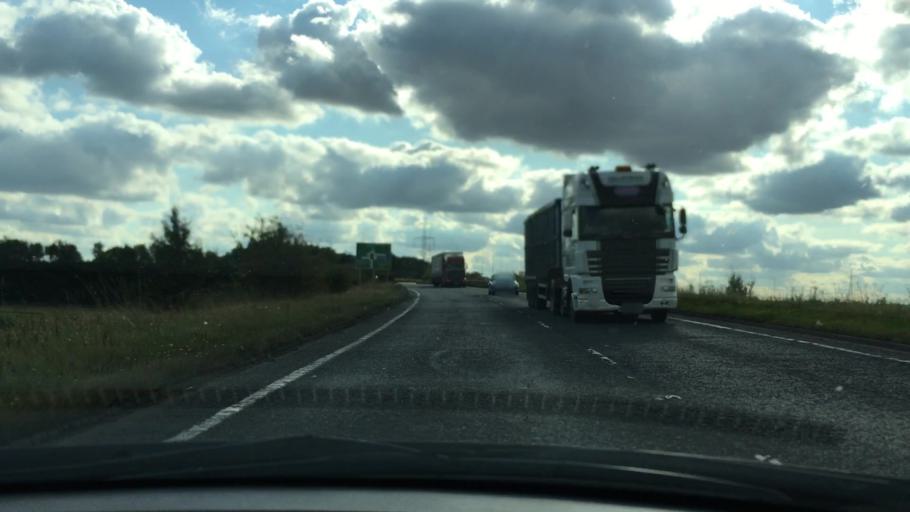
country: GB
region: England
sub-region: North East Lincolnshire
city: Immingham
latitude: 53.6001
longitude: -0.1952
